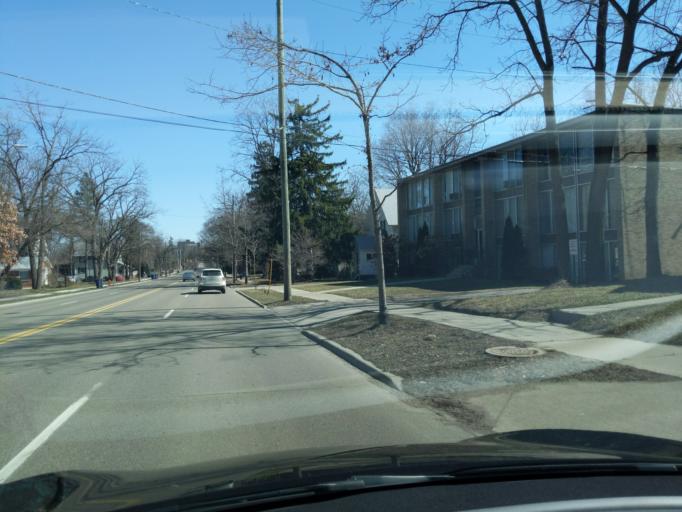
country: US
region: Michigan
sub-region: Washtenaw County
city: Ann Arbor
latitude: 42.2818
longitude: -83.7622
